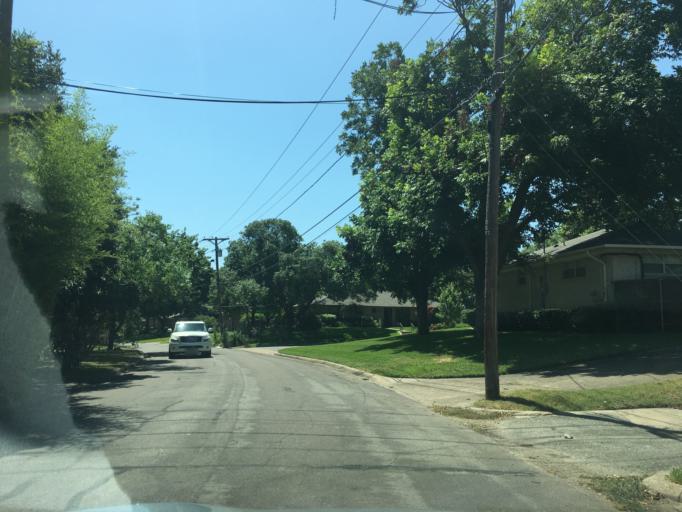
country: US
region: Texas
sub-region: Dallas County
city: Highland Park
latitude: 32.8409
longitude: -96.7501
